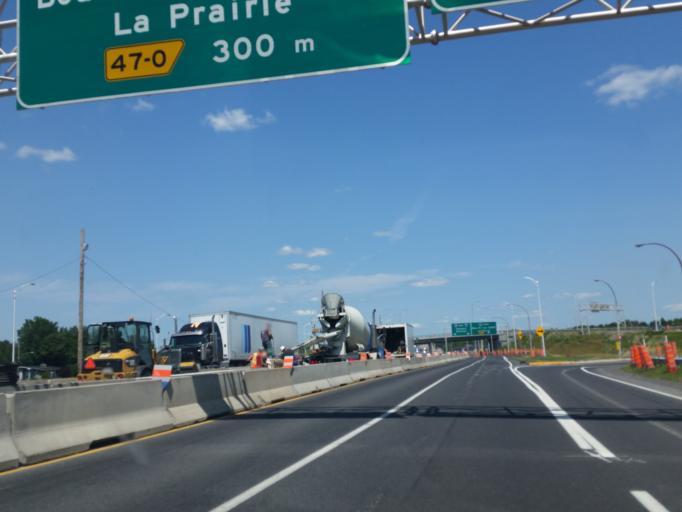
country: CA
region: Quebec
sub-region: Monteregie
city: Saint-Jean-sur-Richelieu
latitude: 45.3432
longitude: -73.2879
